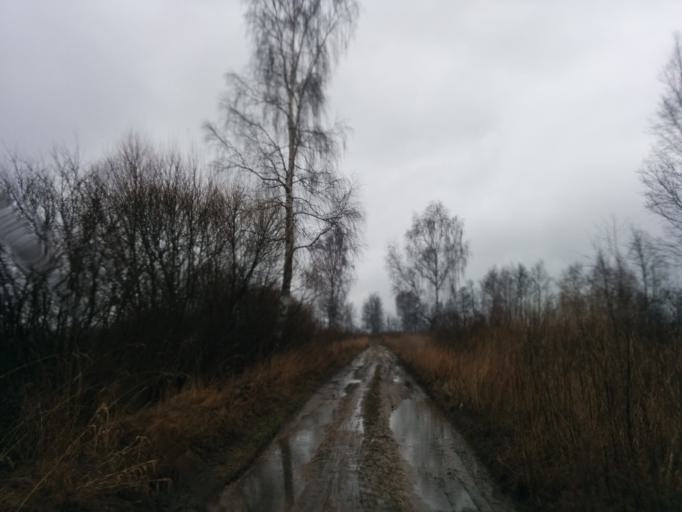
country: LV
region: Jelgava
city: Jelgava
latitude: 56.6742
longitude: 23.7110
